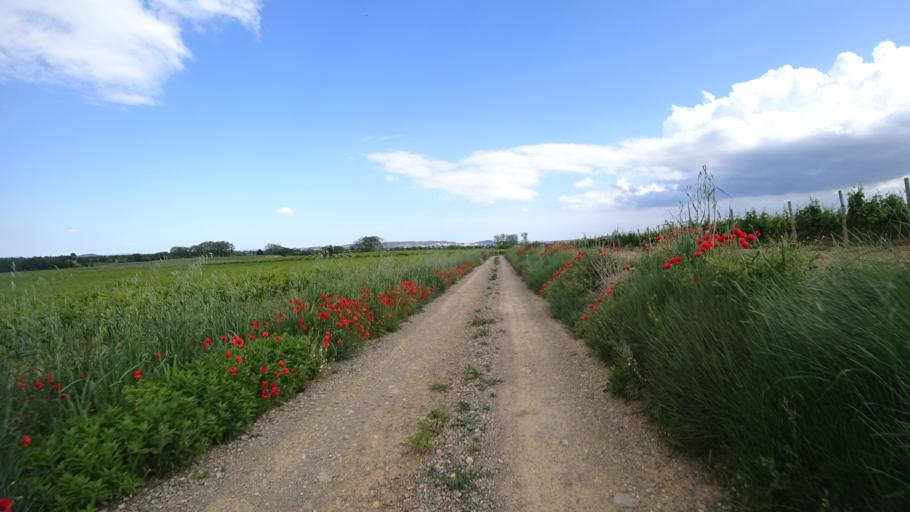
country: FR
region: Languedoc-Roussillon
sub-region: Departement de l'Aude
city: Ginestas
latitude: 43.2549
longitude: 2.8781
